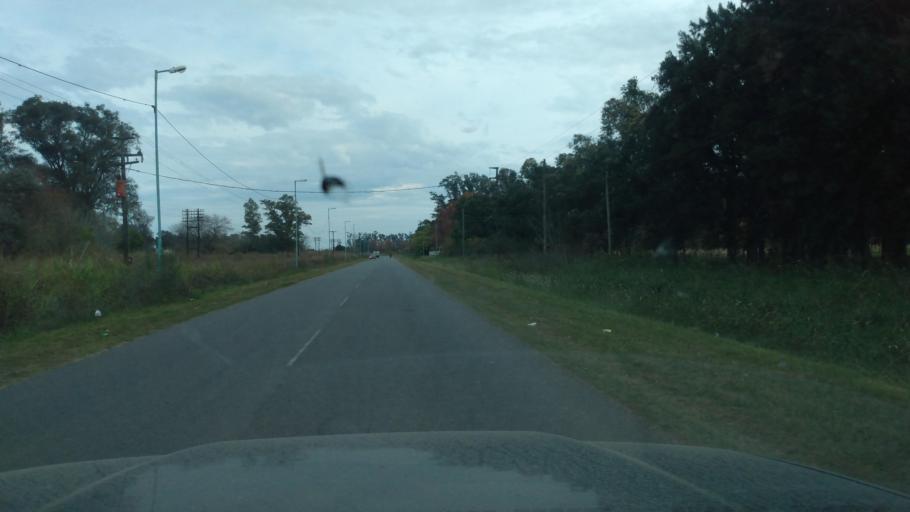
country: AR
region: Buenos Aires
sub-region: Partido de Lujan
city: Lujan
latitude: -34.5948
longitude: -59.1556
